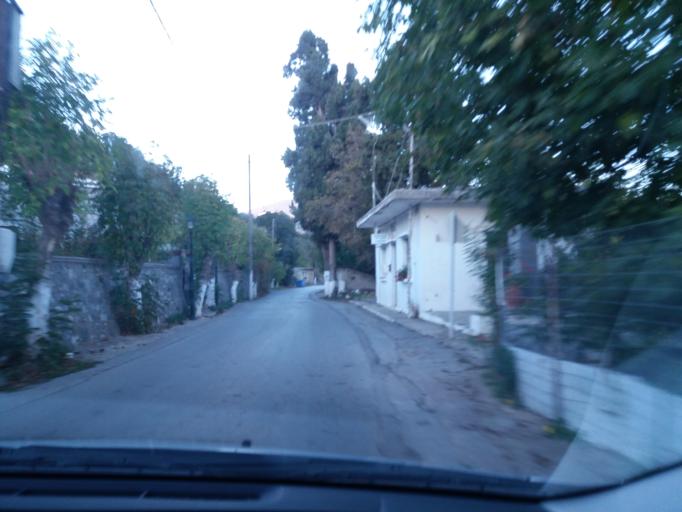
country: GR
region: Crete
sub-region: Nomos Irakleiou
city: Mokhos
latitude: 35.1999
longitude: 25.4711
